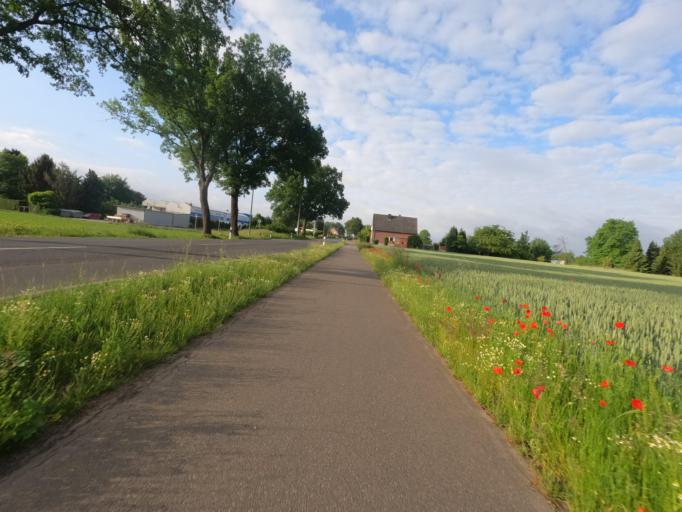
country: DE
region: North Rhine-Westphalia
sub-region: Regierungsbezirk Koln
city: Heinsberg
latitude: 51.0809
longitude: 6.1011
